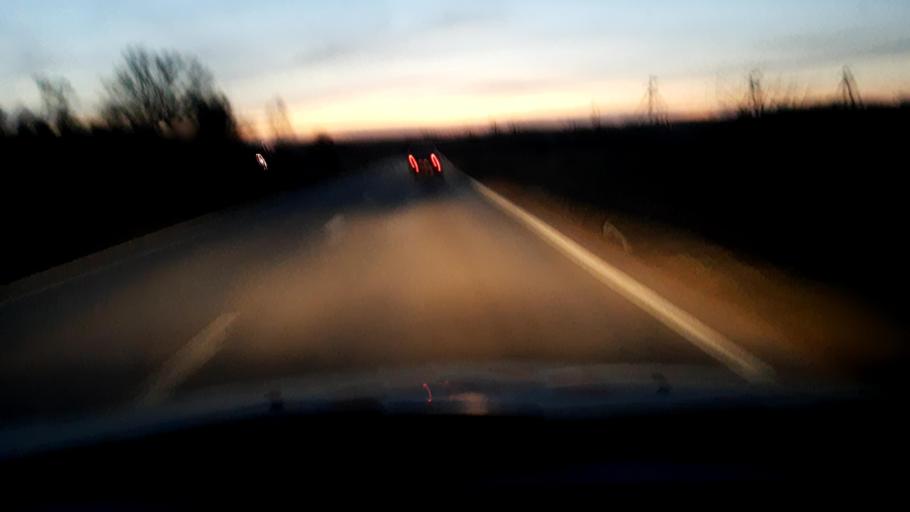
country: RU
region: Bashkortostan
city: Iglino
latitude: 54.7421
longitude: 56.2228
